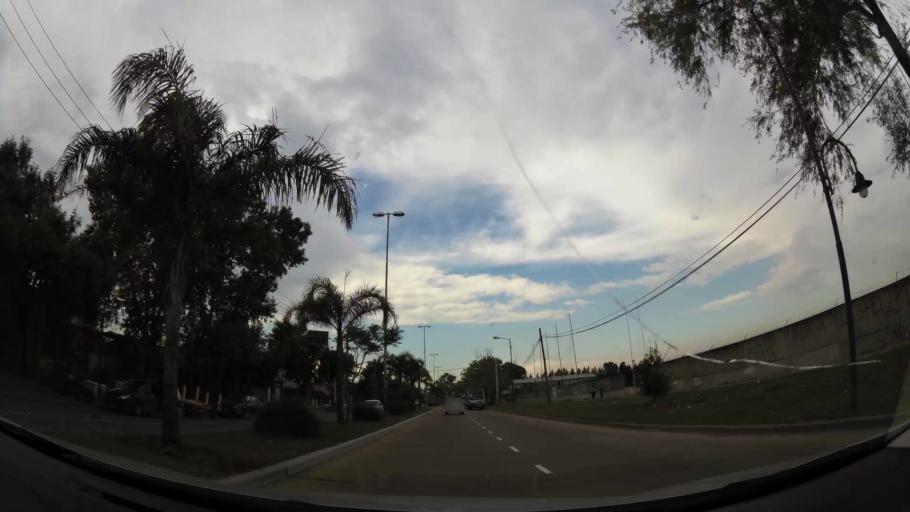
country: AR
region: Buenos Aires
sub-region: Partido de Tigre
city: Tigre
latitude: -34.4783
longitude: -58.6004
